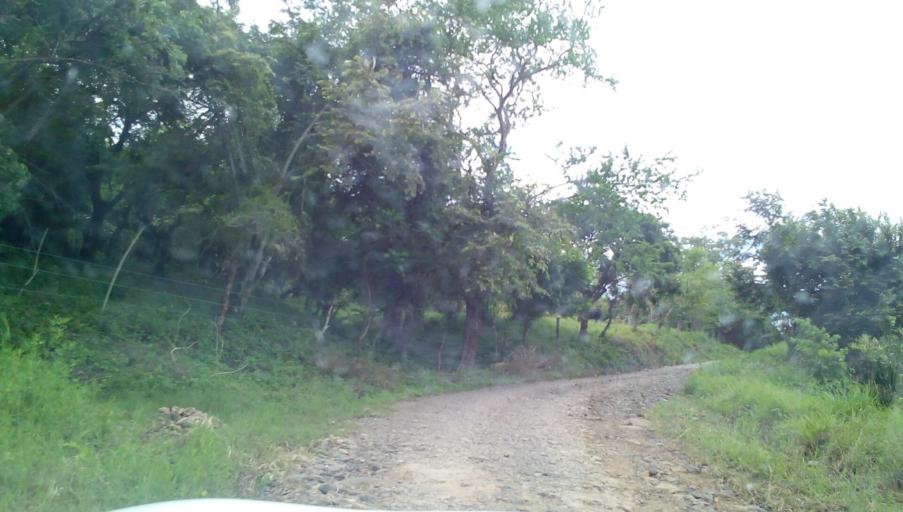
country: MX
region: Veracruz
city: Tepetzintla
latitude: 21.1328
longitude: -97.8508
